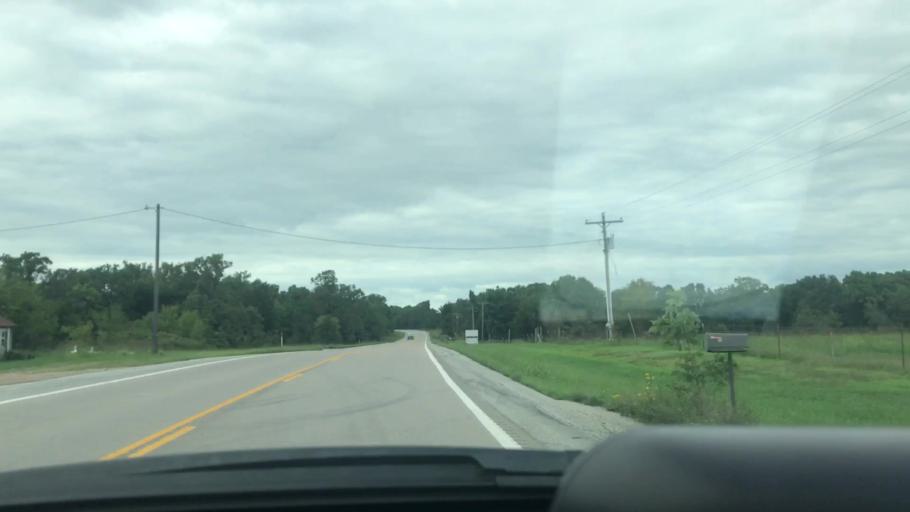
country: US
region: Missouri
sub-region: Benton County
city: Warsaw
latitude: 38.1549
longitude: -93.2965
